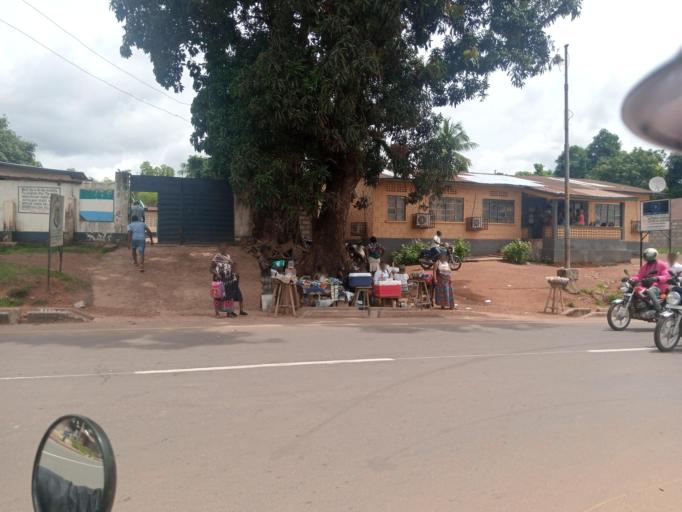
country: SL
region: Southern Province
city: Bo
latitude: 7.9542
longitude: -11.7195
